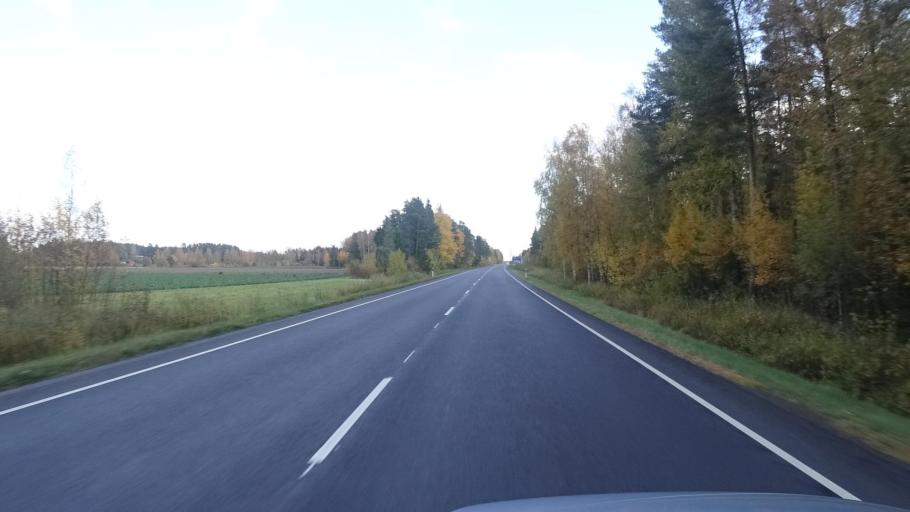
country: FI
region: Satakunta
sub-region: Rauma
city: Koeylioe
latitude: 61.0841
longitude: 22.2661
